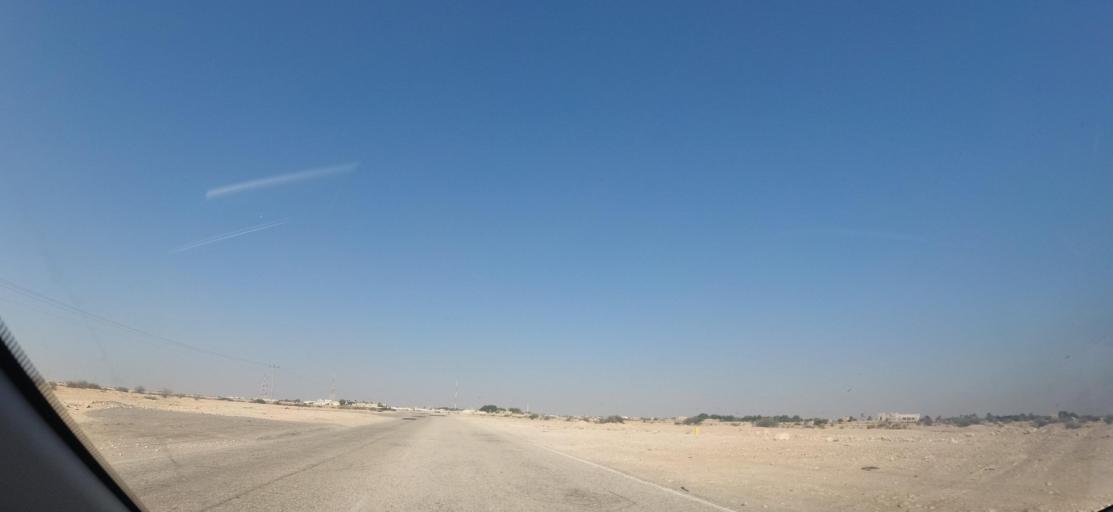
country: QA
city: Al Jumayliyah
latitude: 25.6084
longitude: 51.0775
